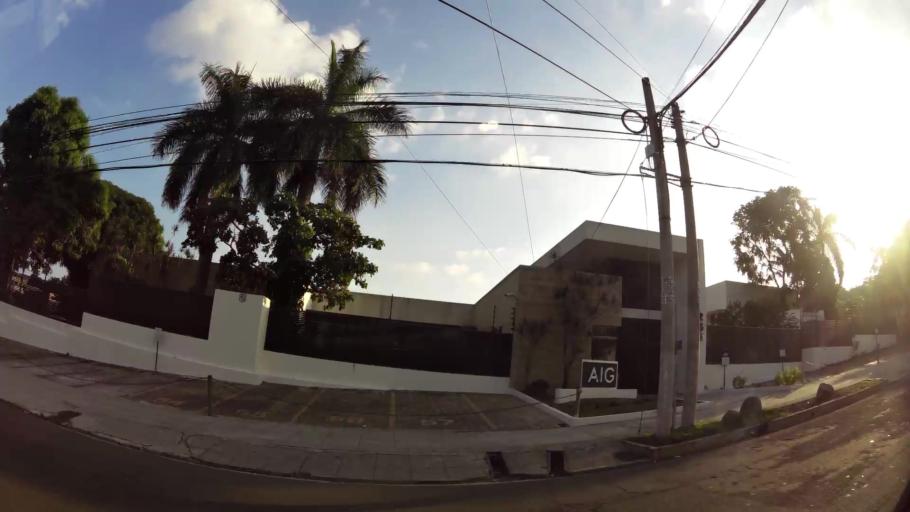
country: SV
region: La Libertad
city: Antiguo Cuscatlan
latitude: 13.6953
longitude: -89.2338
